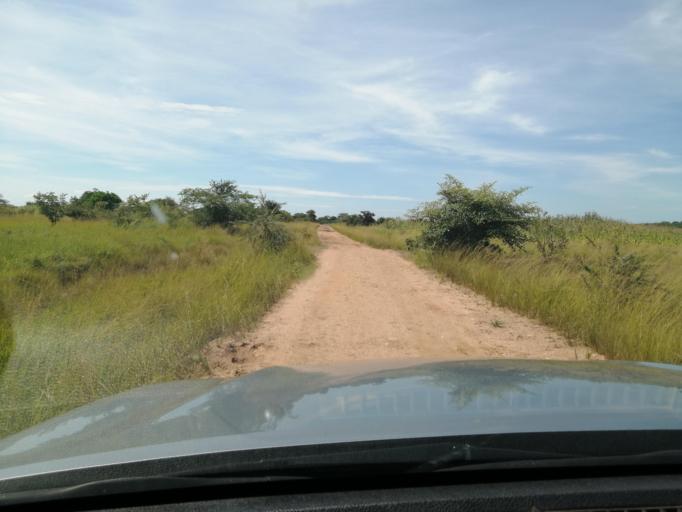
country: ZM
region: Central
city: Chibombo
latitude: -14.9914
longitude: 27.8139
